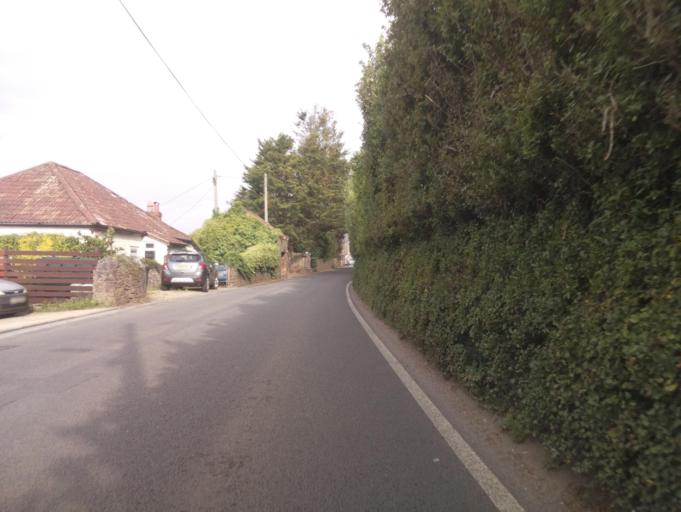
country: GB
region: England
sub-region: North Somerset
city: Nailsea
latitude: 51.4416
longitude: -2.7298
